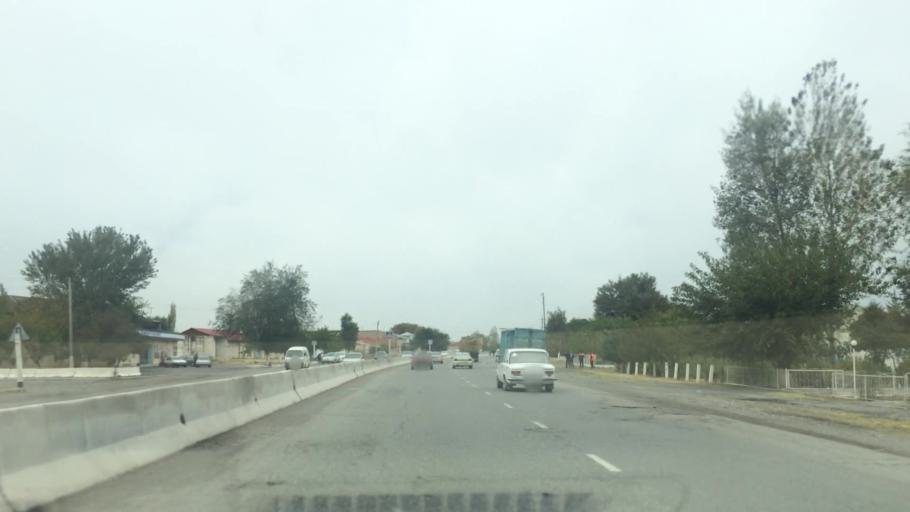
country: UZ
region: Samarqand
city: Bulung'ur
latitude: 39.7719
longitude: 67.2769
